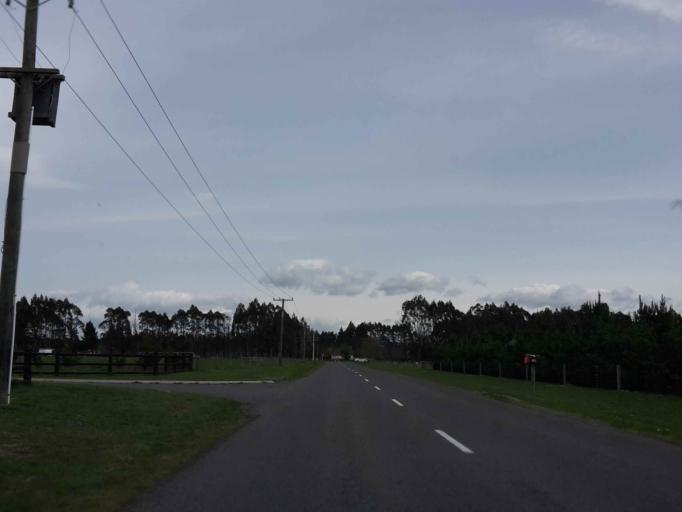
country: NZ
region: Canterbury
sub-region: Waimakariri District
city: Kaiapoi
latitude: -43.3492
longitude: 172.5058
